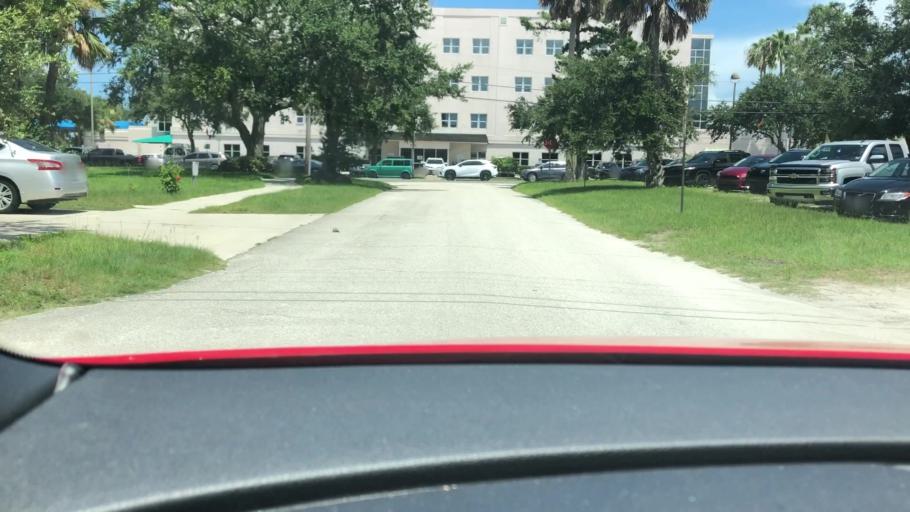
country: US
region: Florida
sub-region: Volusia County
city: New Smyrna Beach
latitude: 29.0205
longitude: -80.9233
